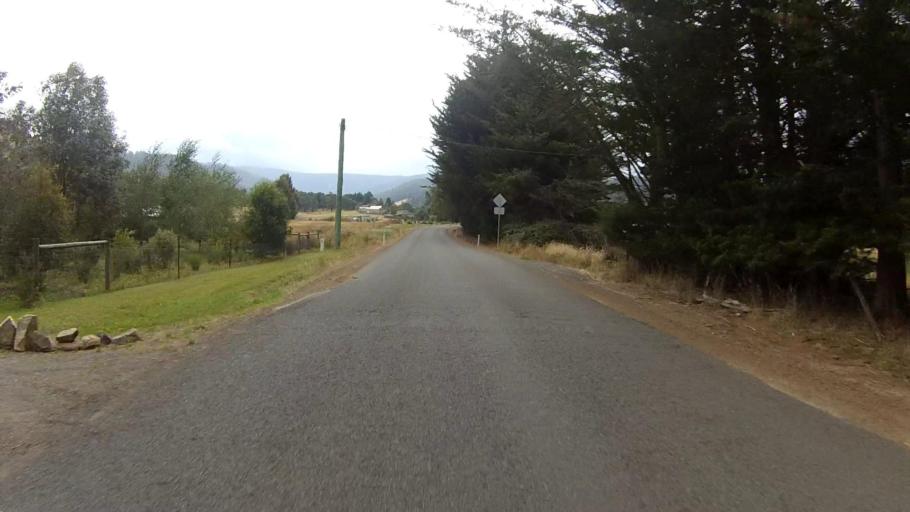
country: AU
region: Tasmania
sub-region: Huon Valley
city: Huonville
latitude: -42.9852
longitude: 147.0585
